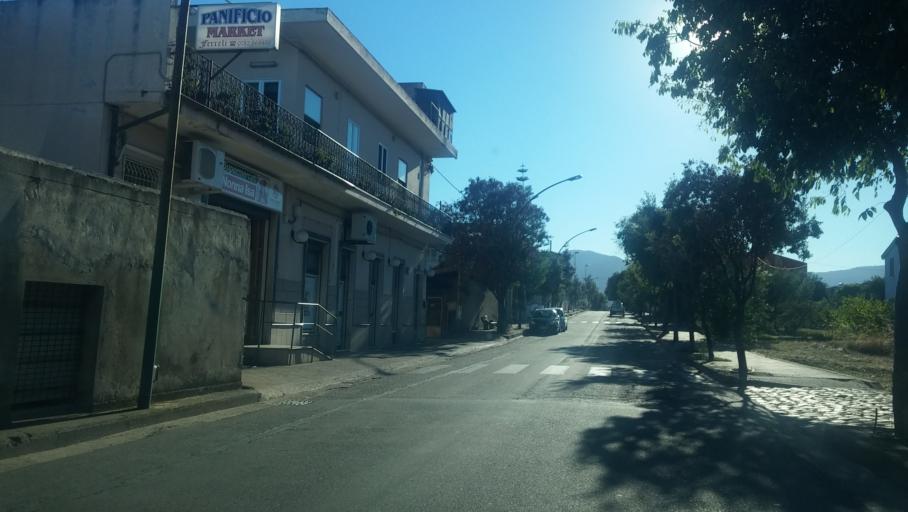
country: IT
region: Sardinia
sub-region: Provincia di Ogliastra
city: Lotzorai
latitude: 39.9689
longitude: 9.6585
